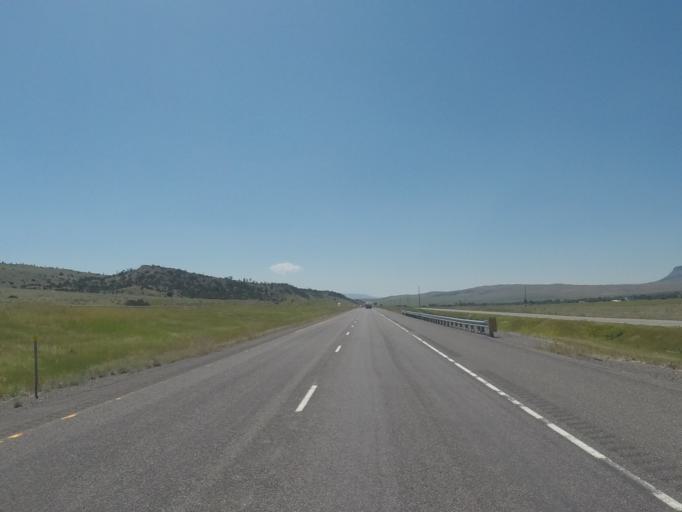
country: US
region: Montana
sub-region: Sweet Grass County
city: Big Timber
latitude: 45.7418
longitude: -110.1969
